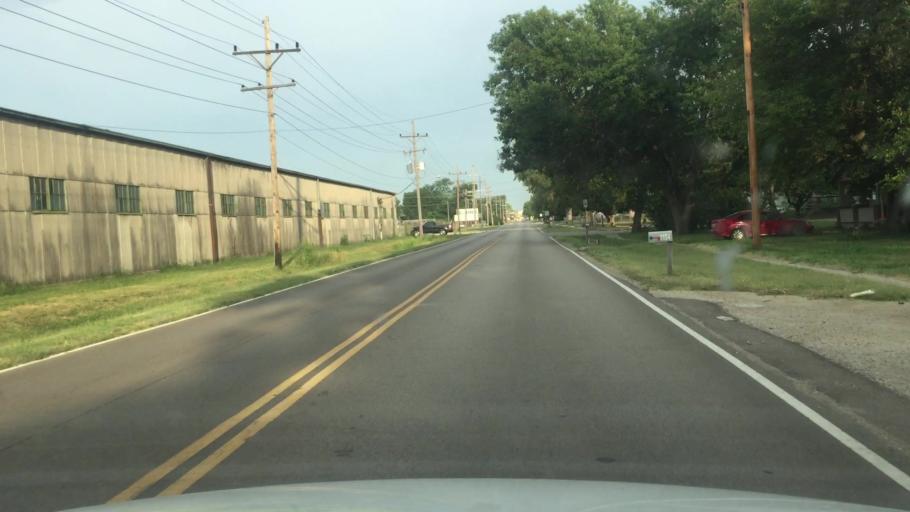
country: US
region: Kansas
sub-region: Shawnee County
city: Topeka
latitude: 39.0589
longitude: -95.6343
